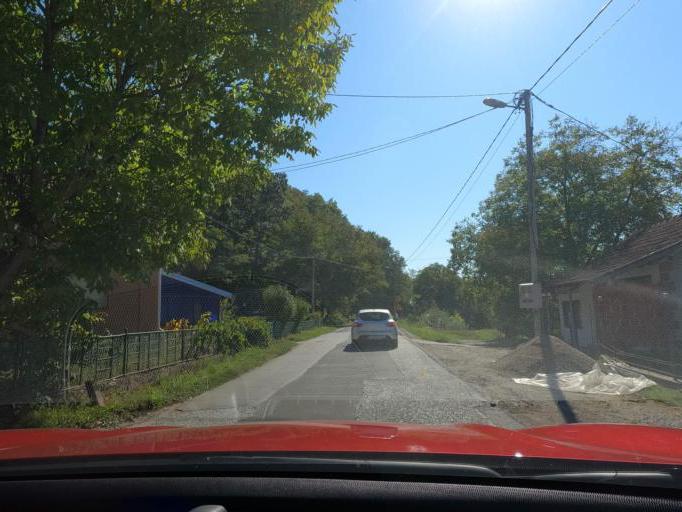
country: RS
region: Central Serbia
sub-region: Raski Okrug
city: Kraljevo
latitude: 43.7375
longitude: 20.7387
